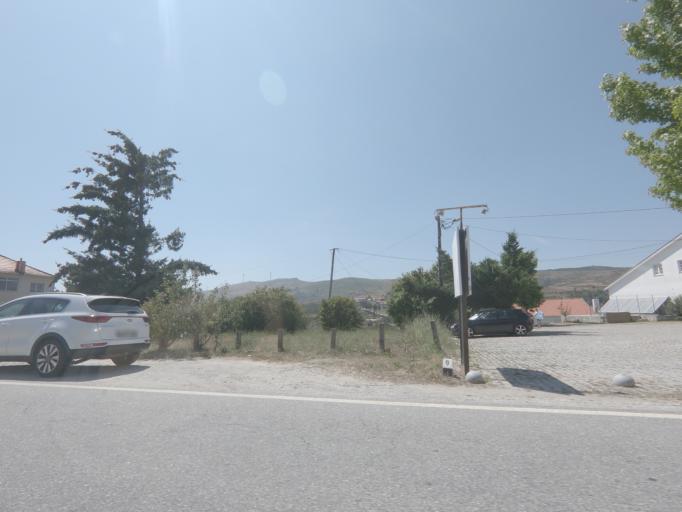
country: PT
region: Viseu
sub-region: Castro Daire
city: Castro Daire
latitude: 40.9794
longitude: -7.8863
